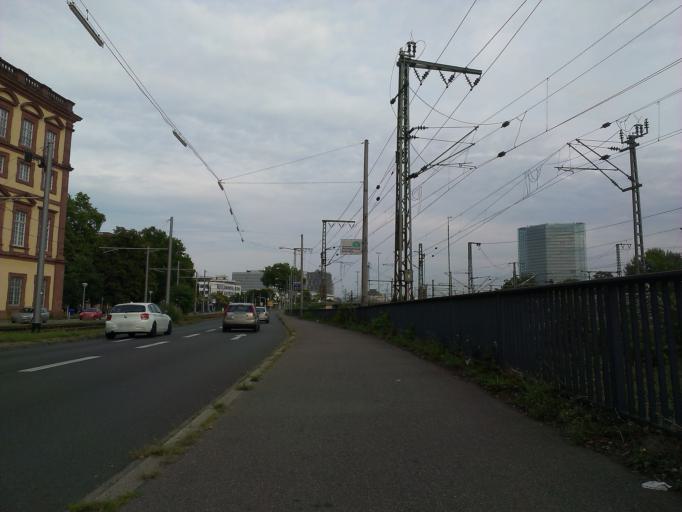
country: DE
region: Rheinland-Pfalz
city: Ludwigshafen am Rhein
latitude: 49.4824
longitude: 8.4616
